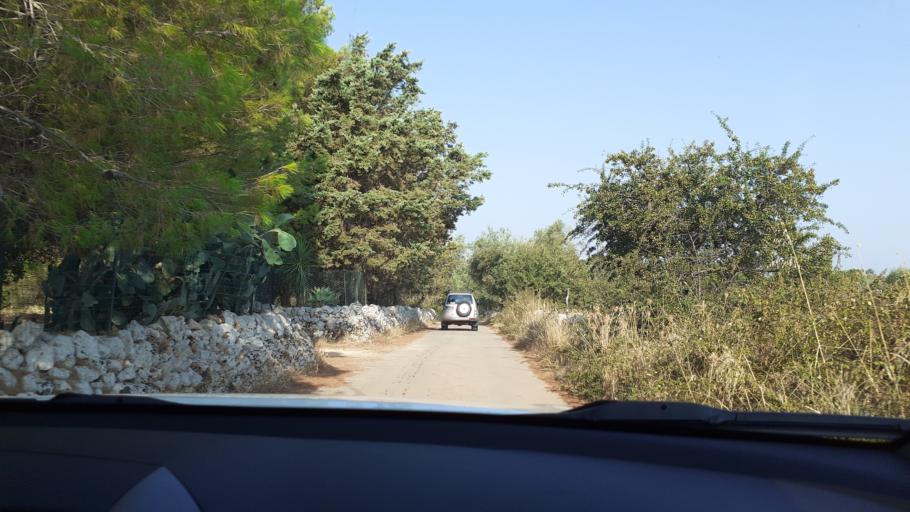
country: IT
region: Sicily
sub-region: Provincia di Siracusa
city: Cassibile
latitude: 36.9809
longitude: 15.1434
